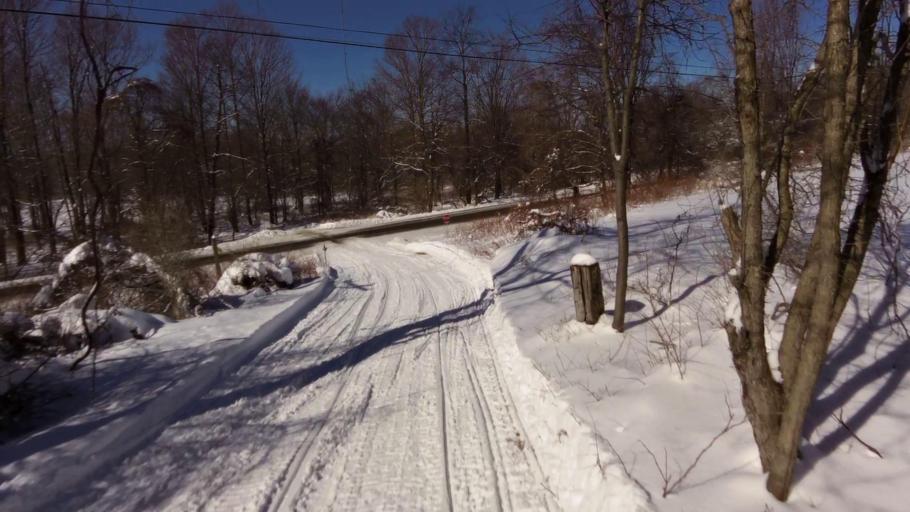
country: US
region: New York
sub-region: Chautauqua County
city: Mayville
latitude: 42.2234
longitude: -79.3978
